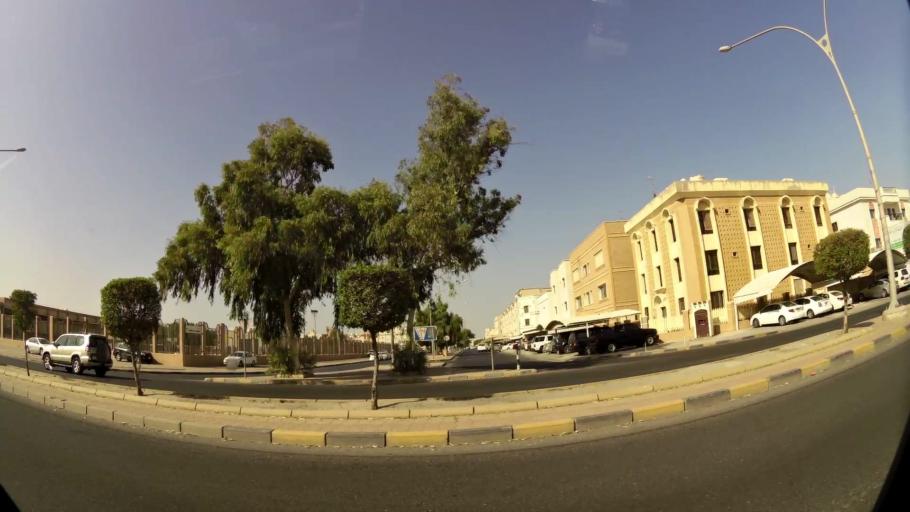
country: KW
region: Muhafazat Hawalli
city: Salwa
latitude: 29.2968
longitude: 48.0816
